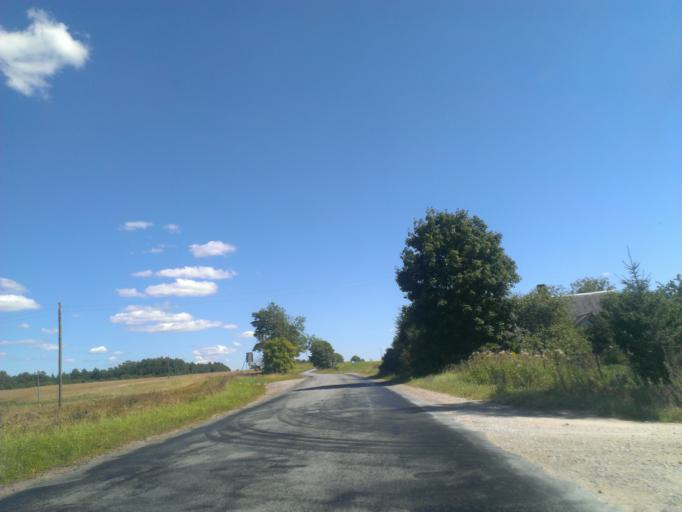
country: LV
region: Malpils
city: Malpils
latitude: 57.0144
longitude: 24.8682
